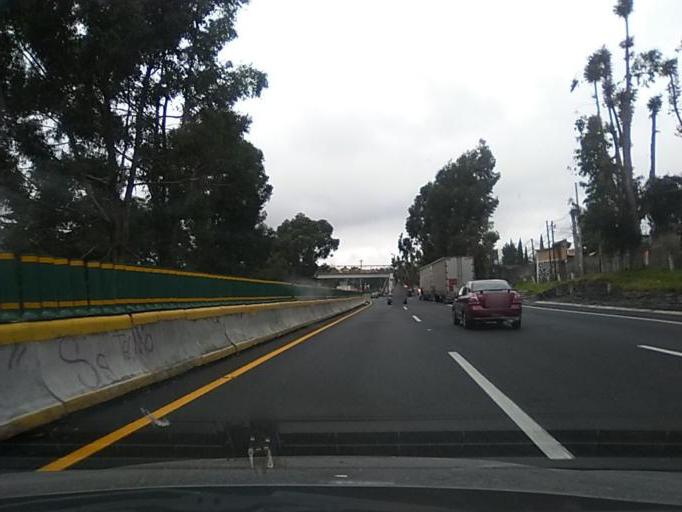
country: MX
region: Mexico City
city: Xochimilco
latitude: 19.2075
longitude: -99.1354
